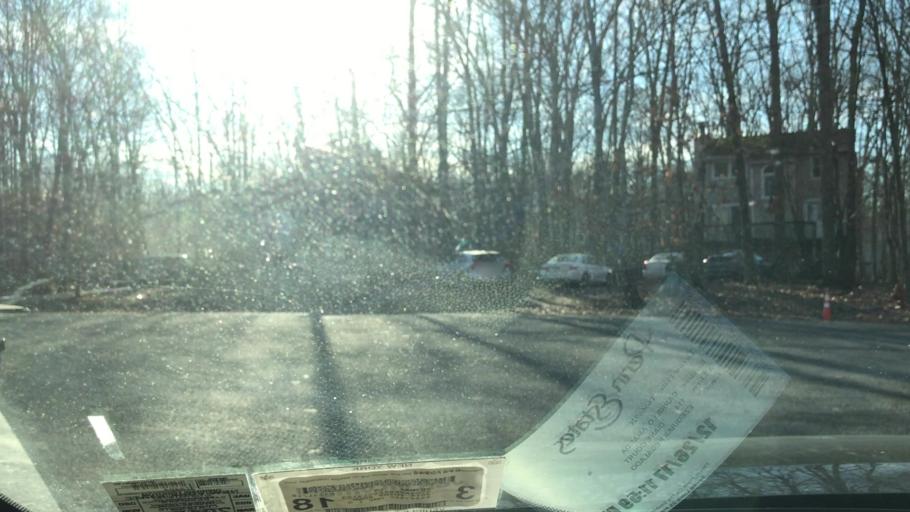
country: US
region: Pennsylvania
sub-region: Monroe County
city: Arlington Heights
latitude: 41.0400
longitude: -75.2468
